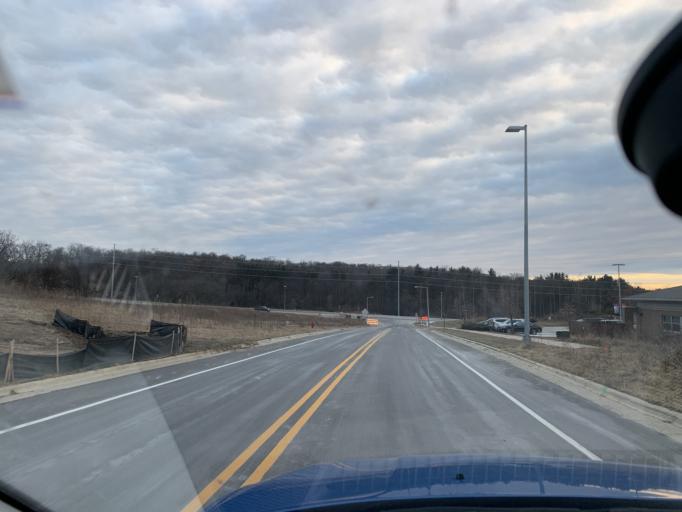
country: US
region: Wisconsin
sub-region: Dane County
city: Verona
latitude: 43.0177
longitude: -89.5268
